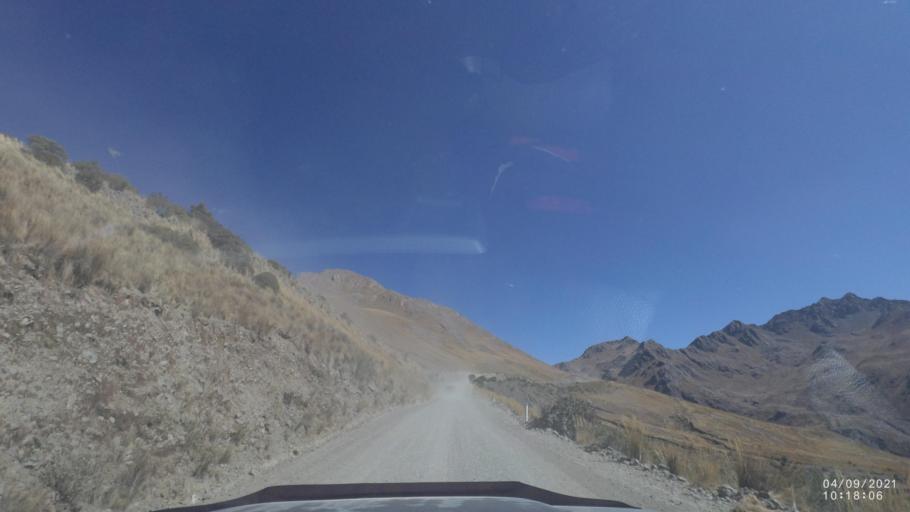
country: BO
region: Cochabamba
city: Sipe Sipe
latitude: -17.3215
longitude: -66.4217
